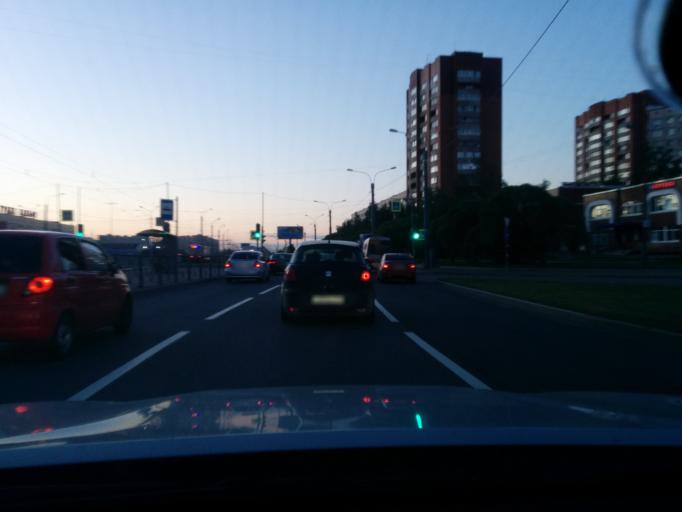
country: RU
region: Leningrad
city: Parnas
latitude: 60.0558
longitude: 30.3374
